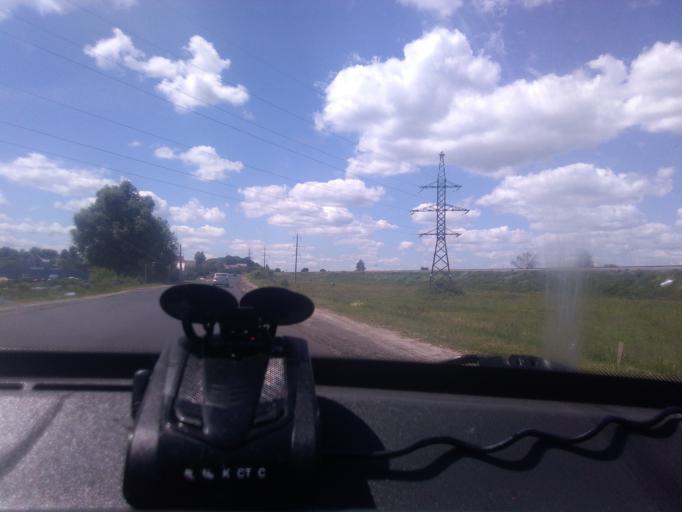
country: RU
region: Kursk
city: Pryamitsyno
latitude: 51.6452
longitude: 35.8966
